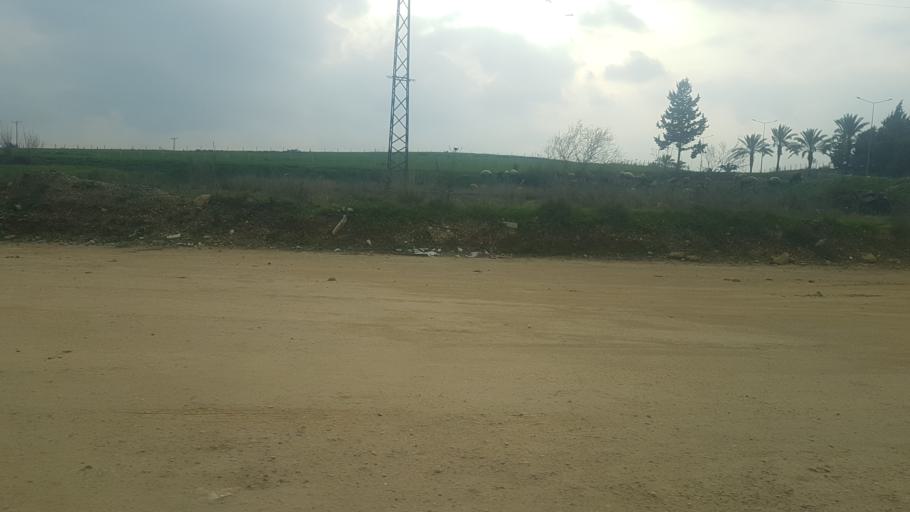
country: TR
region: Adana
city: Seyhan
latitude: 37.0512
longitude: 35.2086
